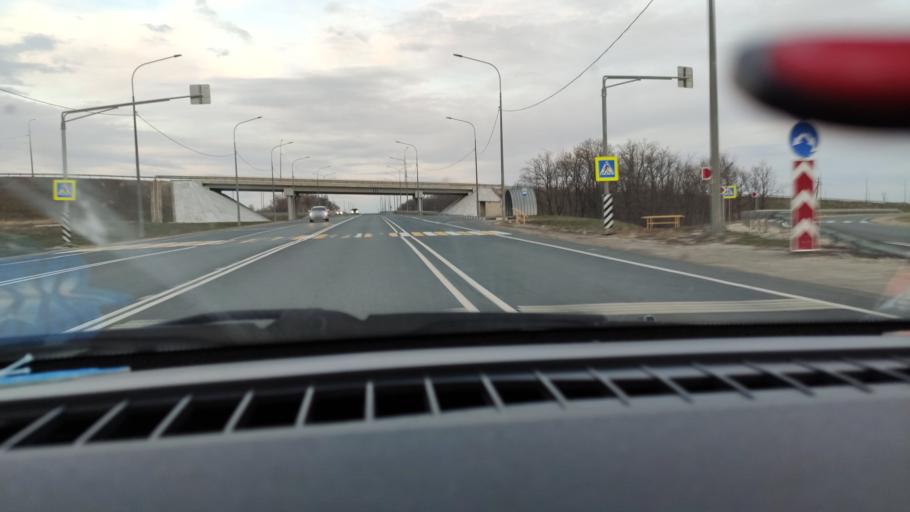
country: RU
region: Saratov
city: Yelshanka
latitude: 51.8246
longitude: 46.3014
